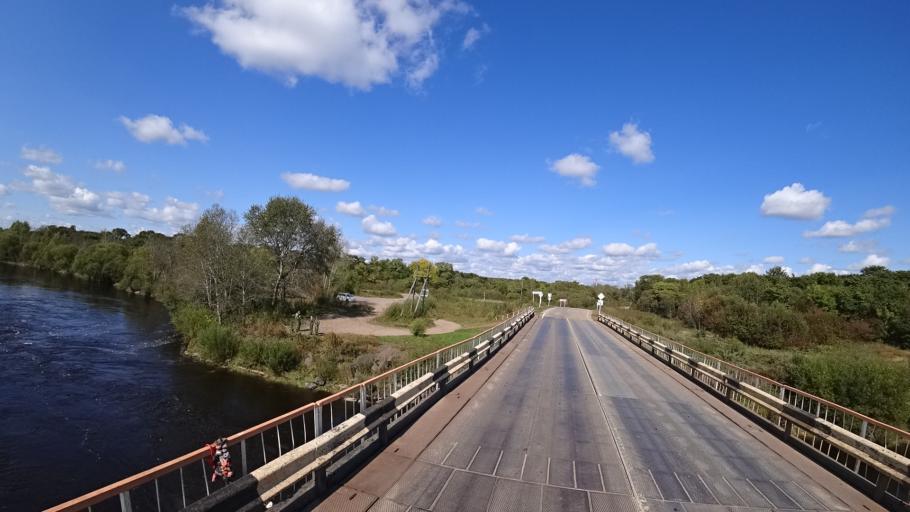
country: RU
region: Amur
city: Arkhara
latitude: 49.3983
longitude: 130.1356
